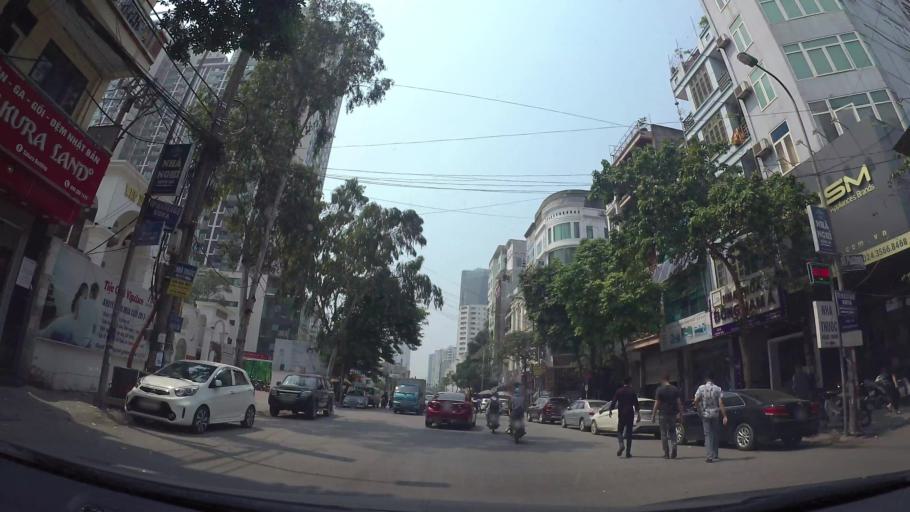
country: VN
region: Ha Noi
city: Thanh Xuan
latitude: 20.9990
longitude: 105.8028
